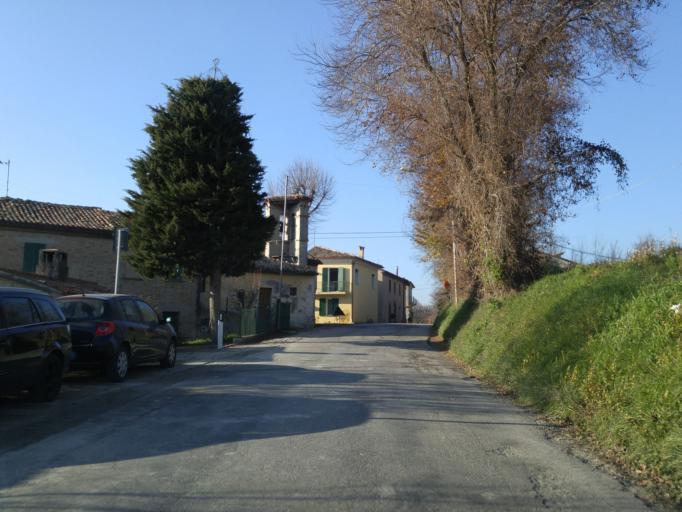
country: IT
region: The Marches
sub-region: Provincia di Pesaro e Urbino
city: Montefelcino
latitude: 43.7282
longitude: 12.8435
